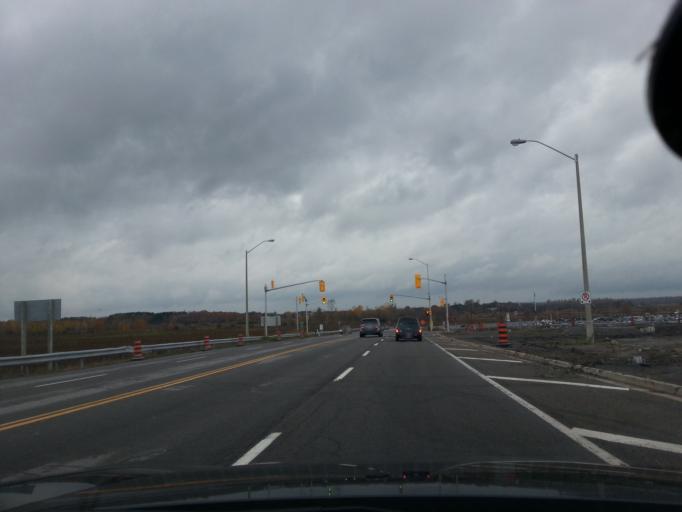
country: CA
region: Ontario
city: Bells Corners
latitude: 45.2943
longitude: -75.9386
